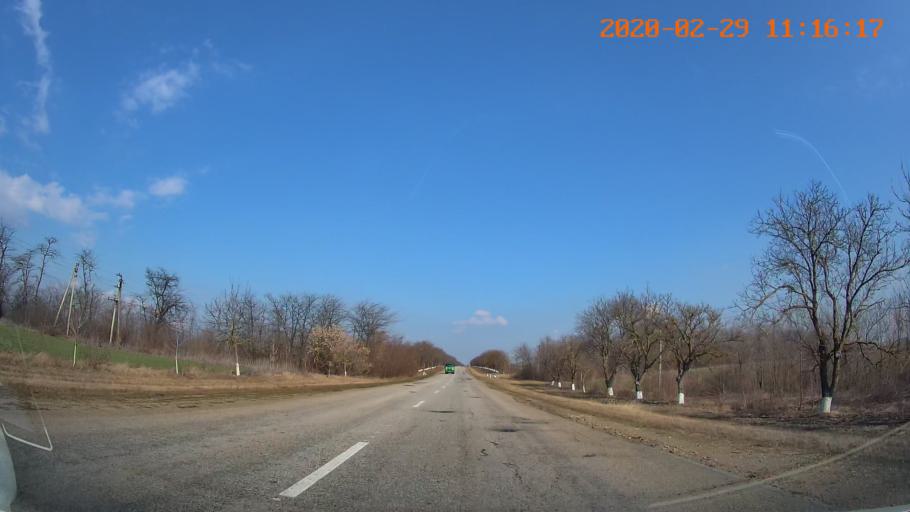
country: MD
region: Telenesti
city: Dubasari
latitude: 47.3066
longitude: 29.1674
